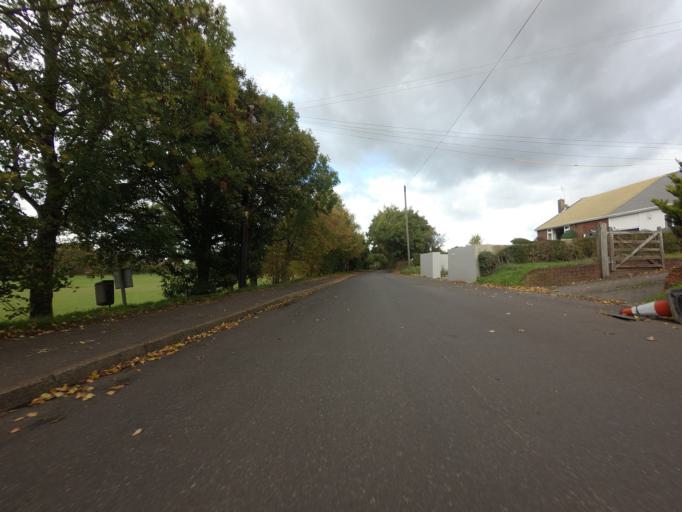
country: GB
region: England
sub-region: Kent
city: Swanley
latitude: 51.3877
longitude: 0.1634
